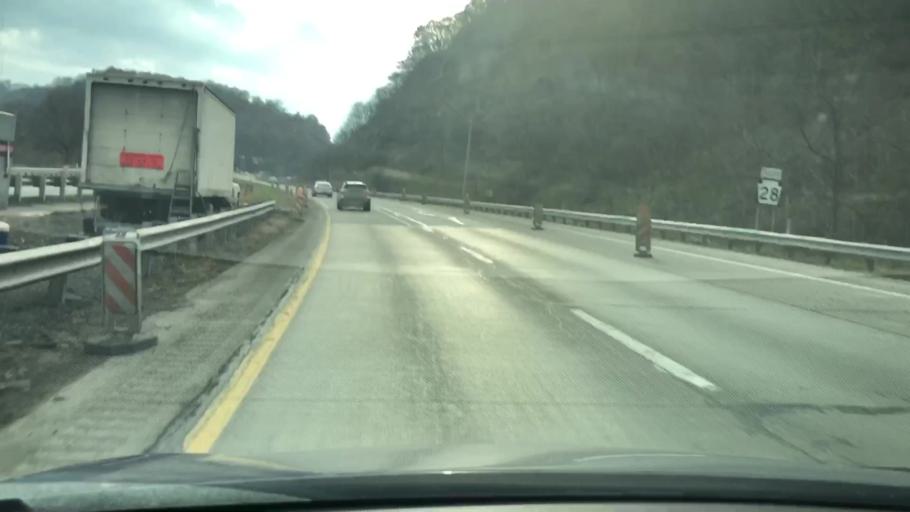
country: US
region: Pennsylvania
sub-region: Westmoreland County
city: Arnold
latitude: 40.5872
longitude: -79.7776
